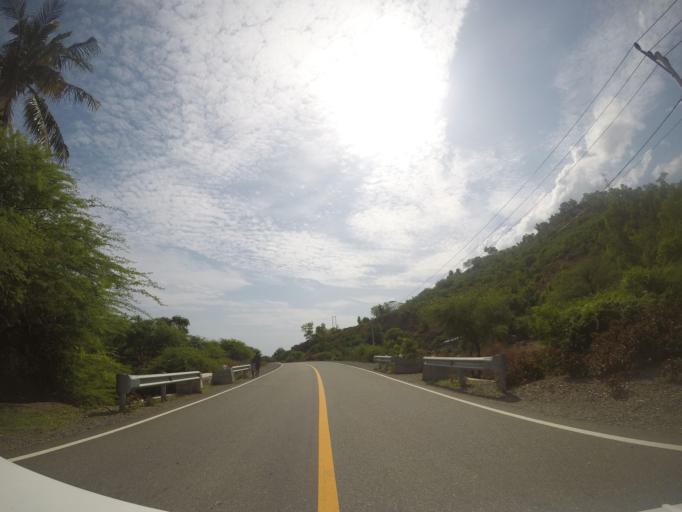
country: ID
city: Metinaro
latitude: -8.4771
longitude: 125.8746
